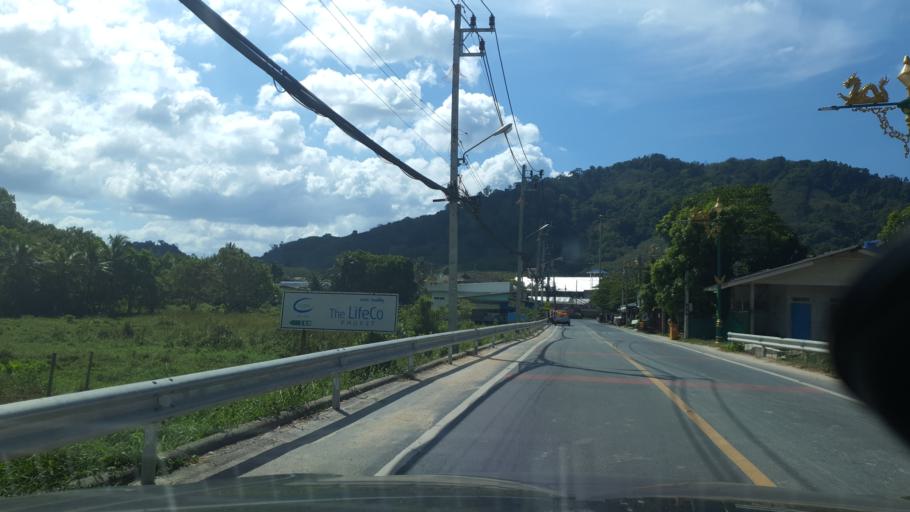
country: TH
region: Phuket
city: Thalang
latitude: 8.0746
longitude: 98.2992
